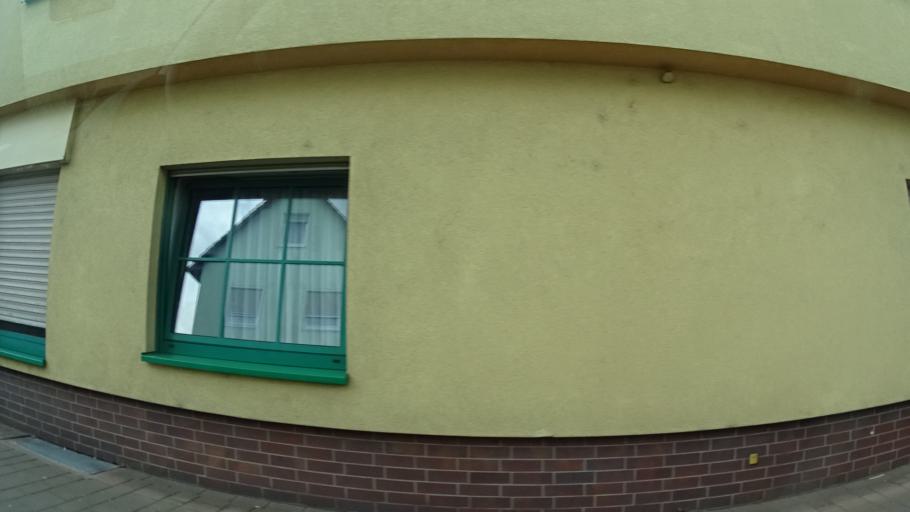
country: DE
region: Bavaria
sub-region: Regierungsbezirk Unterfranken
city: Oberthulba
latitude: 50.1989
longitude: 9.9613
